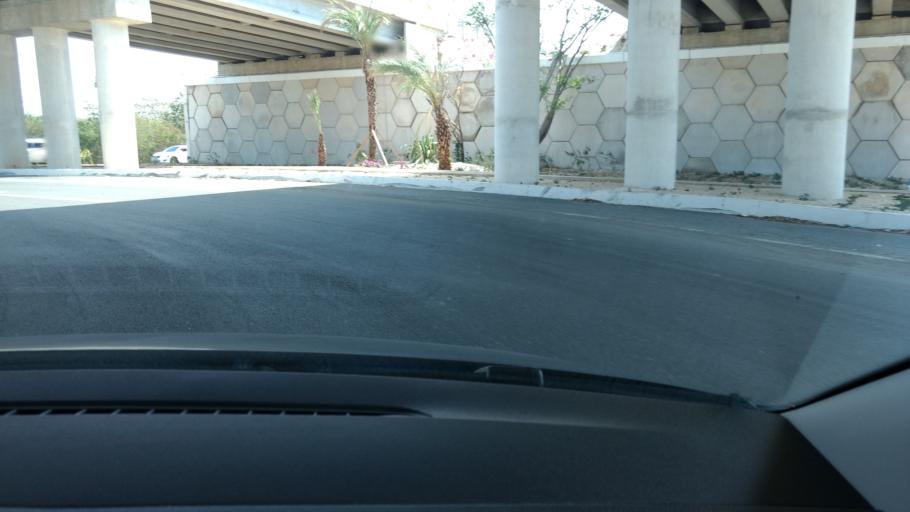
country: MX
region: Yucatan
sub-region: Kanasin
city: Kanasin
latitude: 20.9813
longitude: -89.5641
